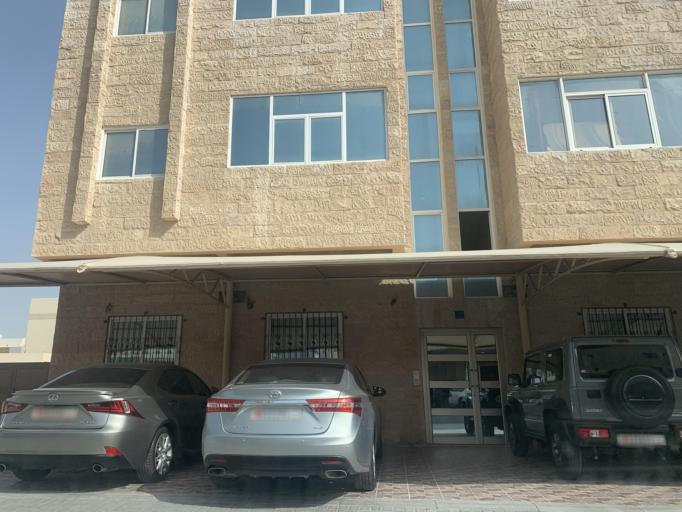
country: BH
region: Northern
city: Madinat `Isa
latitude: 26.1881
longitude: 50.5589
